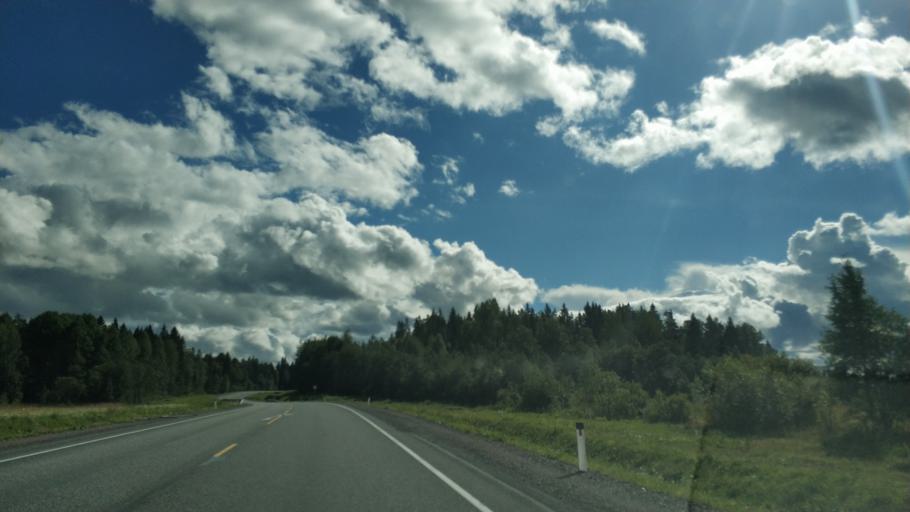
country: RU
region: Republic of Karelia
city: Ruskeala
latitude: 61.8718
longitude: 30.6501
